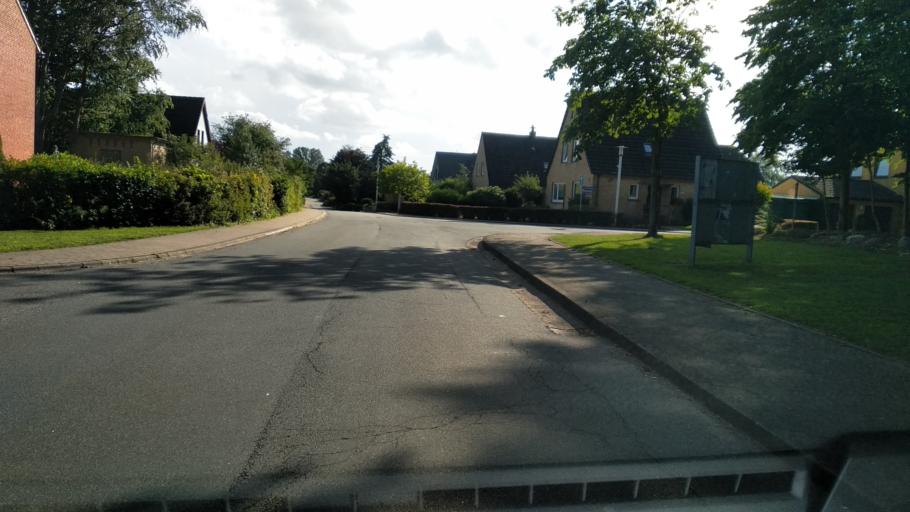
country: DE
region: Schleswig-Holstein
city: Busdorf
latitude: 54.4878
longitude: 9.5460
